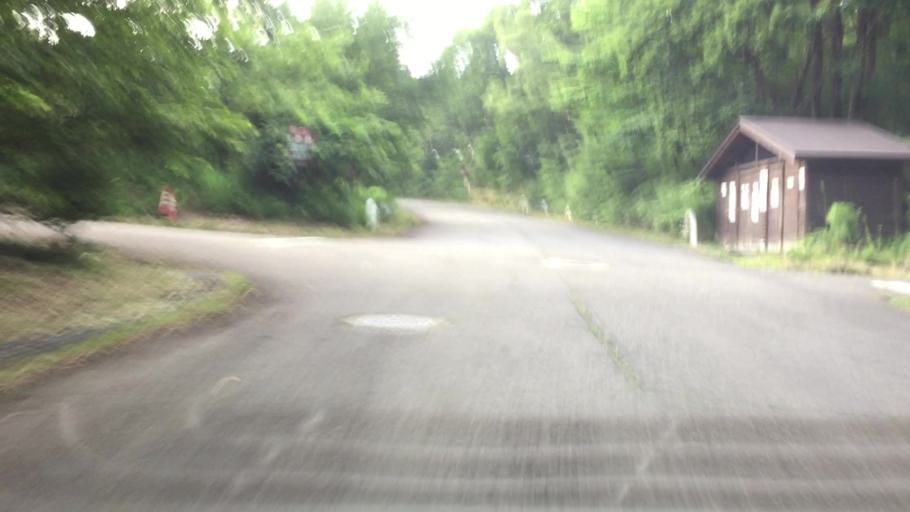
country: JP
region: Tochigi
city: Kuroiso
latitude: 37.1016
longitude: 140.0433
